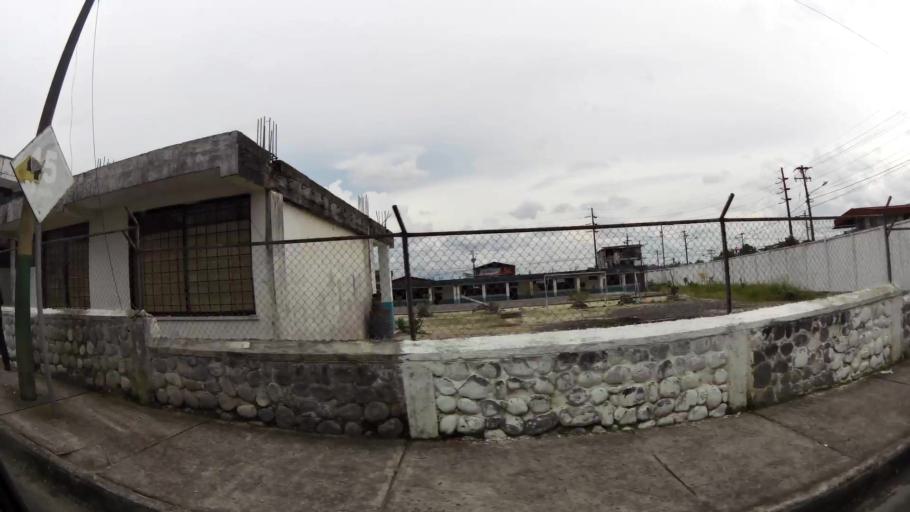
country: EC
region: Pastaza
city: Puyo
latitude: -1.4935
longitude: -78.0136
